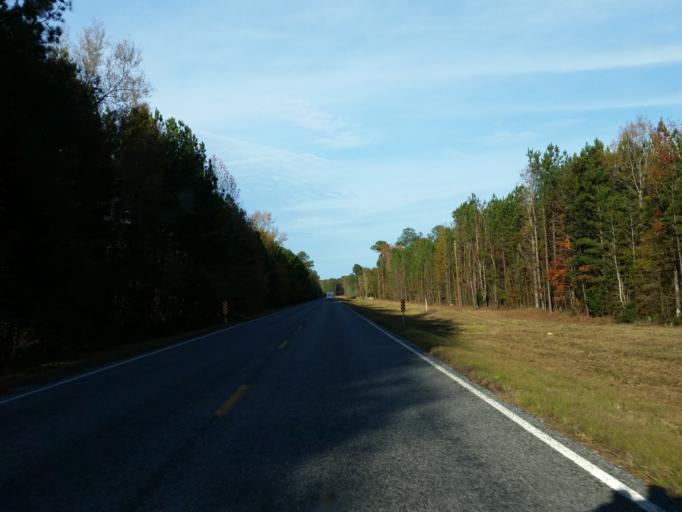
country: US
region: Mississippi
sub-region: Clarke County
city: Stonewall
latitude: 32.0745
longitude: -88.8767
